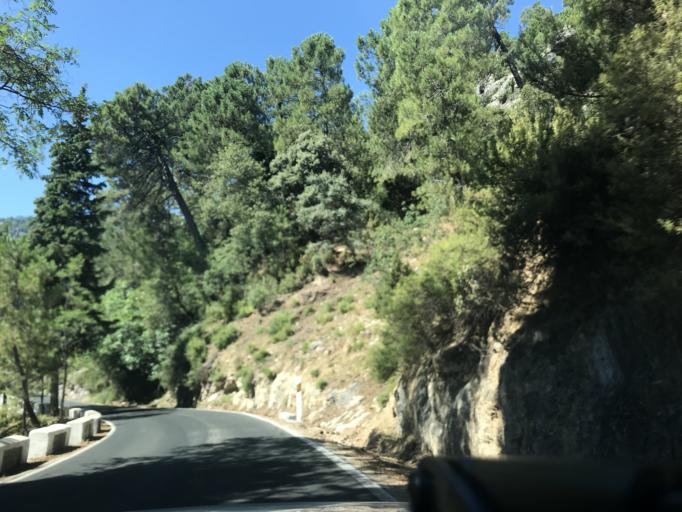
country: ES
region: Andalusia
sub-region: Provincia de Jaen
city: La Iruela
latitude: 37.9251
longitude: -2.9513
